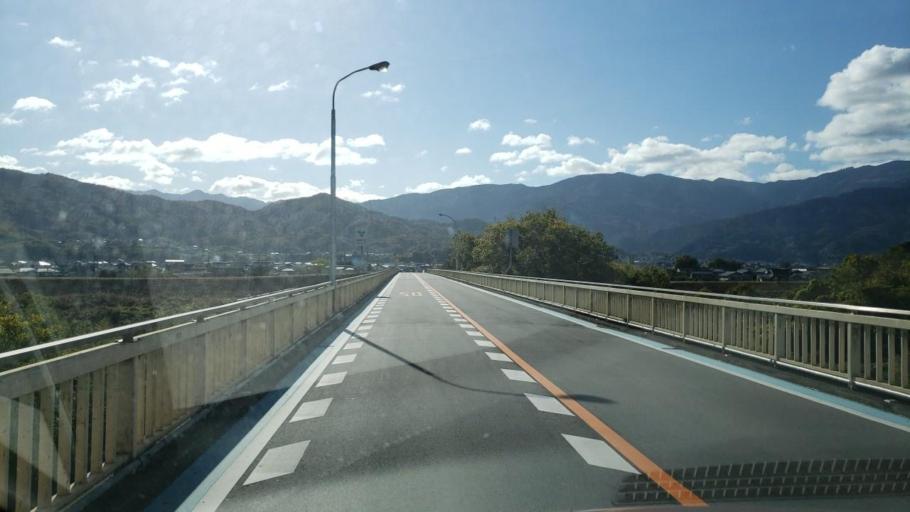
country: JP
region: Tokushima
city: Wakimachi
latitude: 34.0690
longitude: 134.2371
